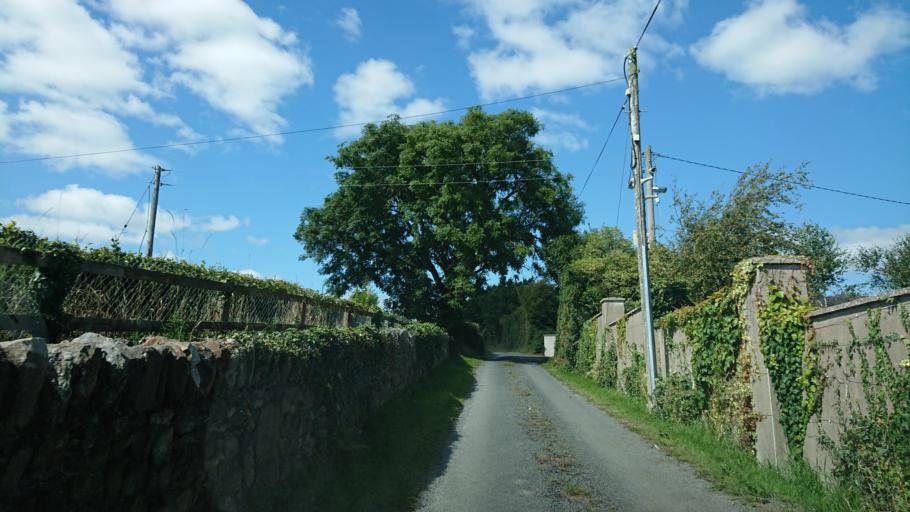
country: IE
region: Munster
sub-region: Waterford
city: Waterford
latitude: 52.2306
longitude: -7.1537
